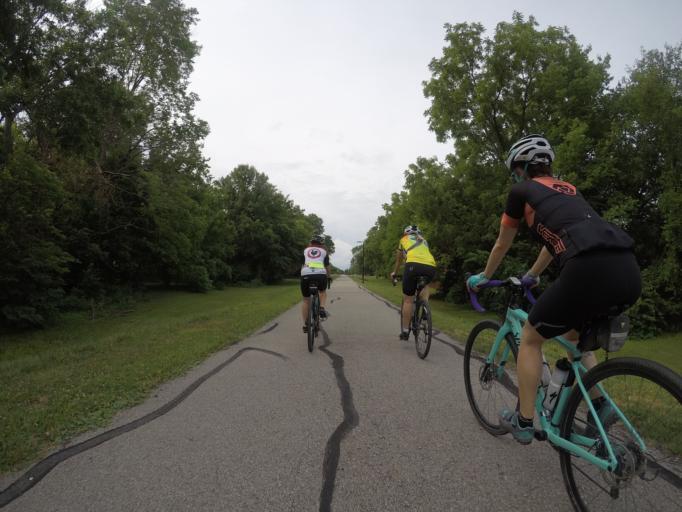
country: US
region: Kansas
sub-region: Franklin County
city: Ottawa
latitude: 38.6065
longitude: -95.2701
